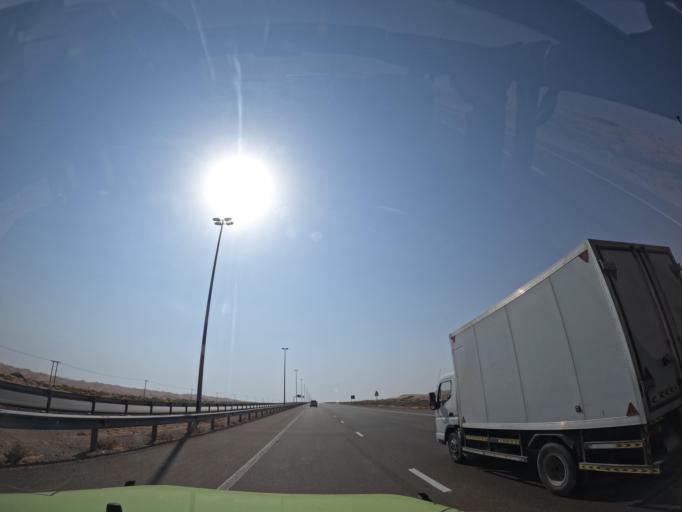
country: OM
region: Al Buraimi
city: Al Buraymi
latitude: 24.4355
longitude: 55.6713
